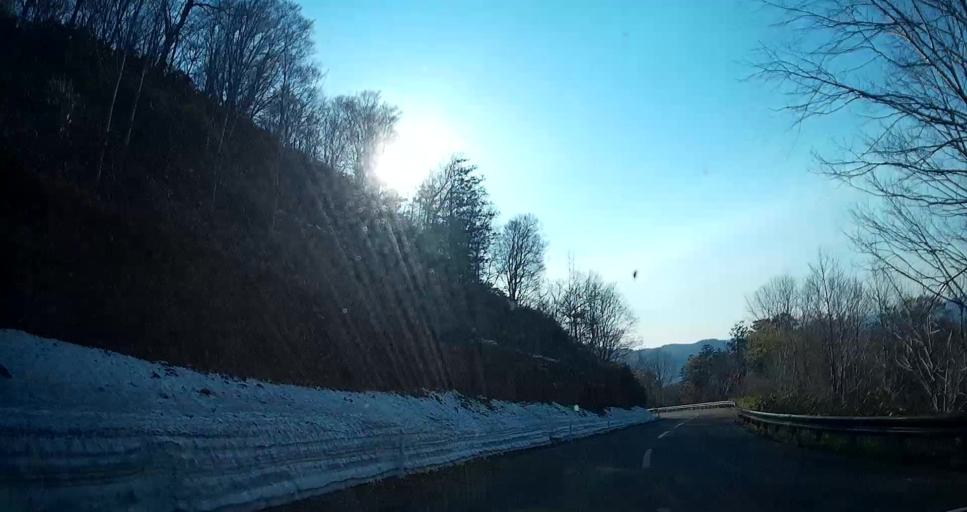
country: JP
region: Aomori
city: Mutsu
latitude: 41.3092
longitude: 141.1193
